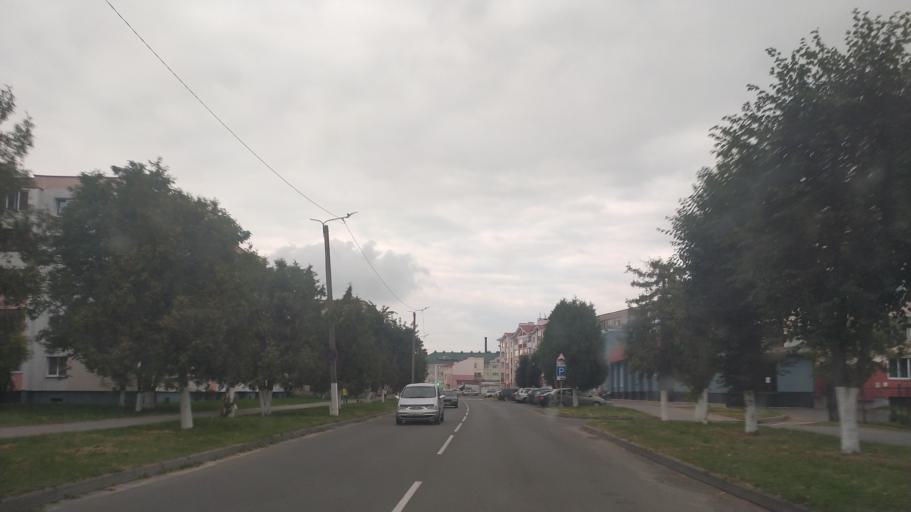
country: BY
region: Brest
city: Byaroza
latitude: 52.5318
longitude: 24.9854
